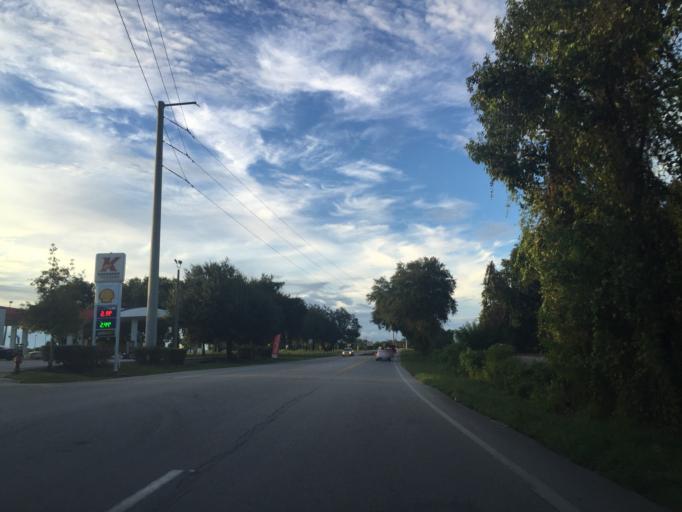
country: US
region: Florida
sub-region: Lake County
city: Tavares
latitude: 28.7826
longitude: -81.7477
